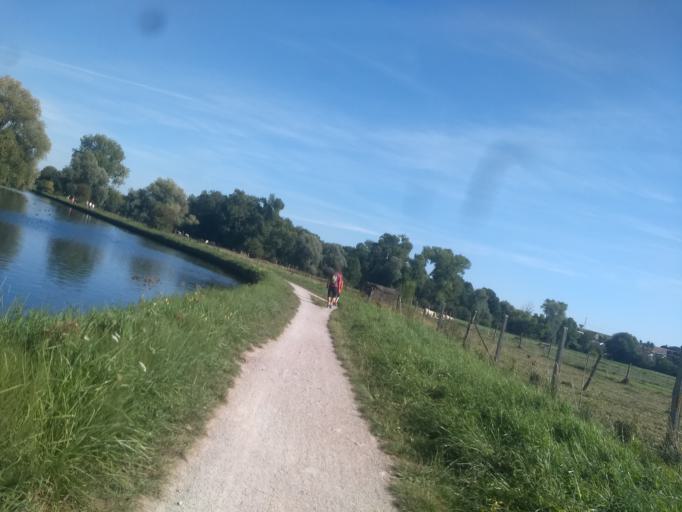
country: FR
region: Nord-Pas-de-Calais
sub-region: Departement du Pas-de-Calais
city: Feuchy
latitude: 50.2962
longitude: 2.8475
